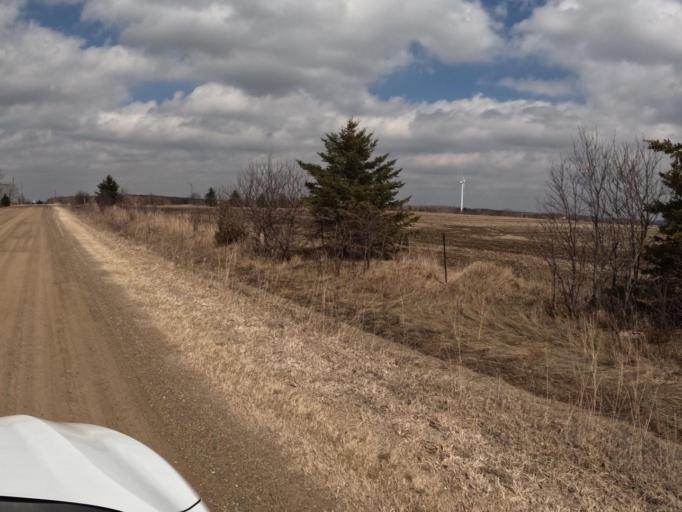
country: CA
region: Ontario
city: Shelburne
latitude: 44.0184
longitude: -80.3290
